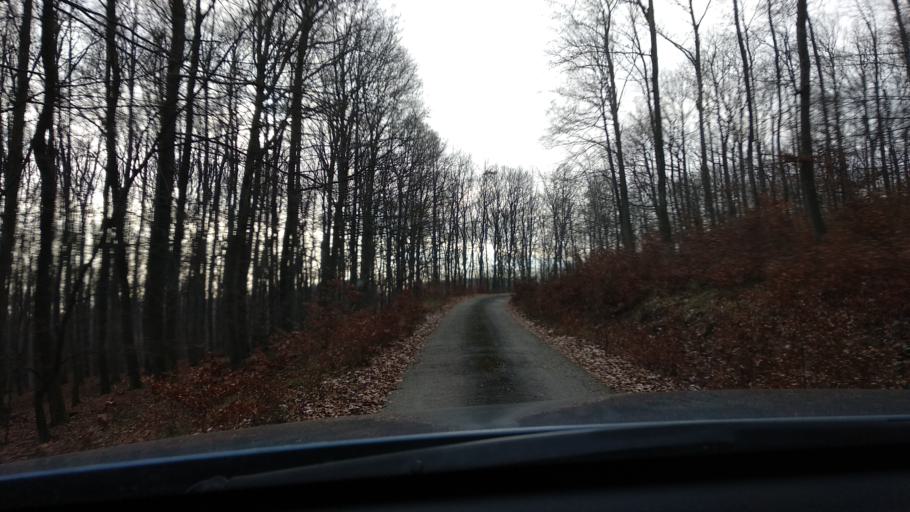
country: SK
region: Trenciansky
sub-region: Okres Trencin
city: Trencin
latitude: 48.8007
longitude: 18.0820
